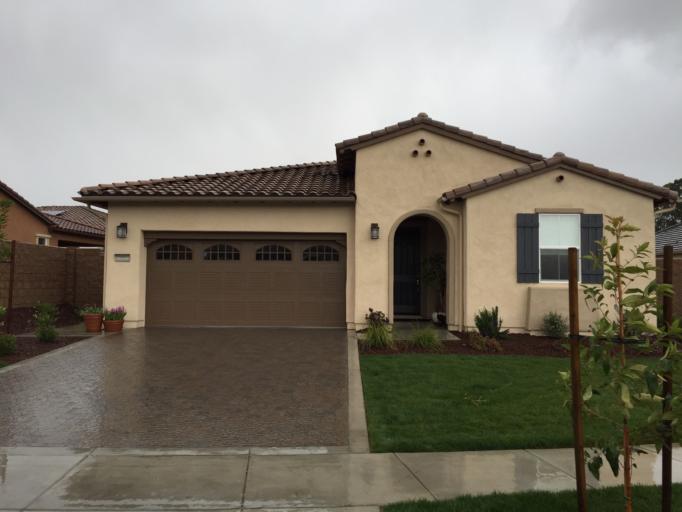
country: US
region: California
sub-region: San Luis Obispo County
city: Callender
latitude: 35.0318
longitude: -120.5461
